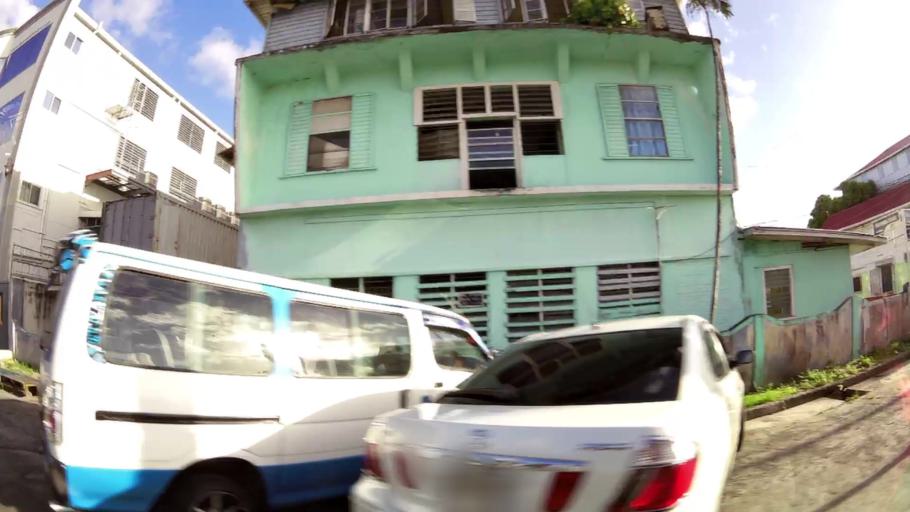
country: GY
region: Demerara-Mahaica
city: Georgetown
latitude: 6.8073
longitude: -58.1569
